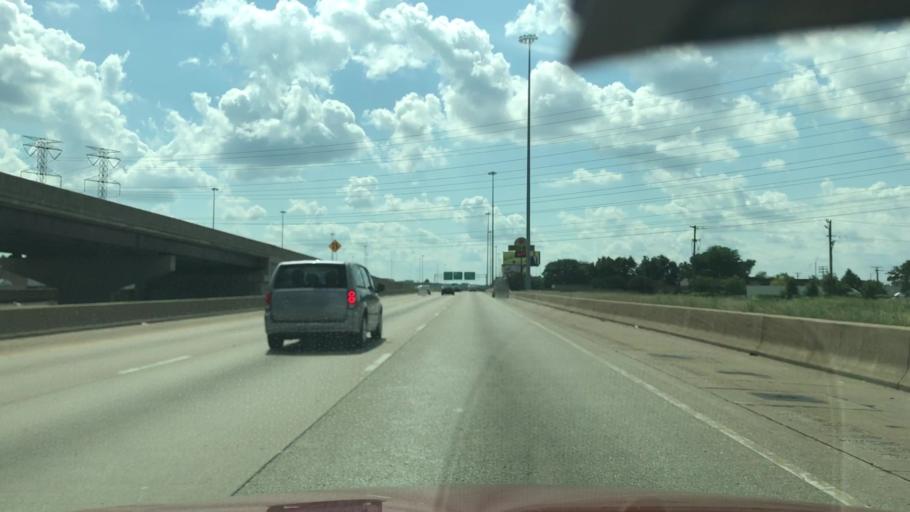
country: US
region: Illinois
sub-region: Cook County
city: Lansing
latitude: 41.5783
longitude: -87.5597
